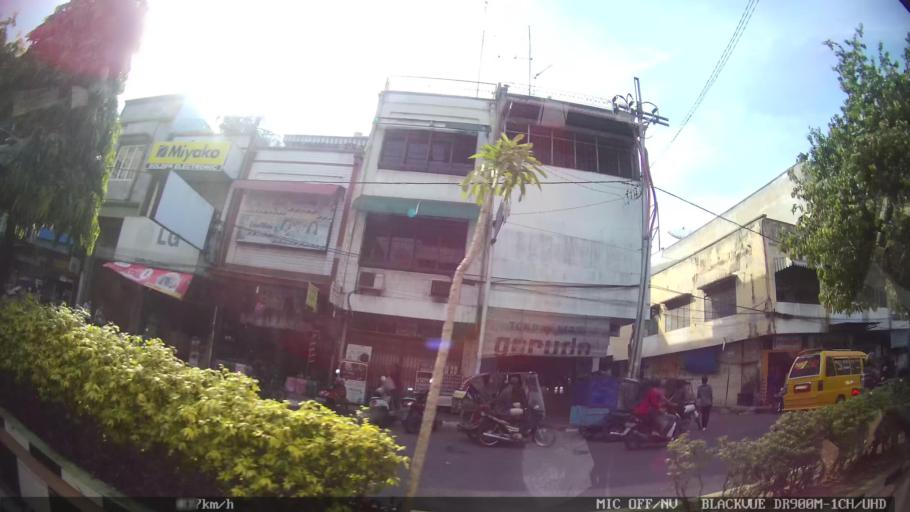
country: ID
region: North Sumatra
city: Binjai
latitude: 3.6064
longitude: 98.4882
